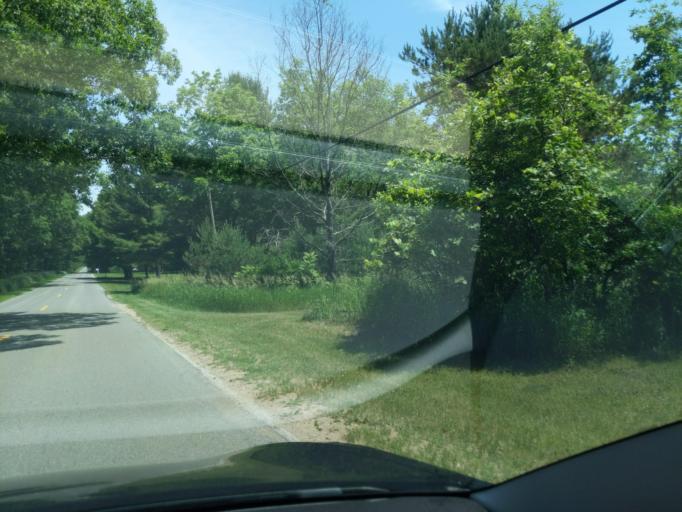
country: US
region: Michigan
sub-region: Muskegon County
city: Montague
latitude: 43.4156
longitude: -86.3918
